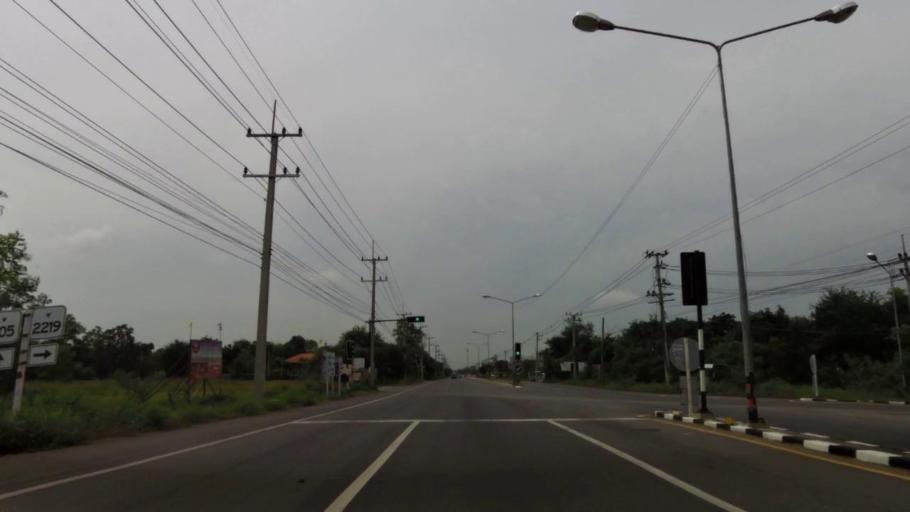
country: TH
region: Lop Buri
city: Ban Mi
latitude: 15.0567
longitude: 100.5884
